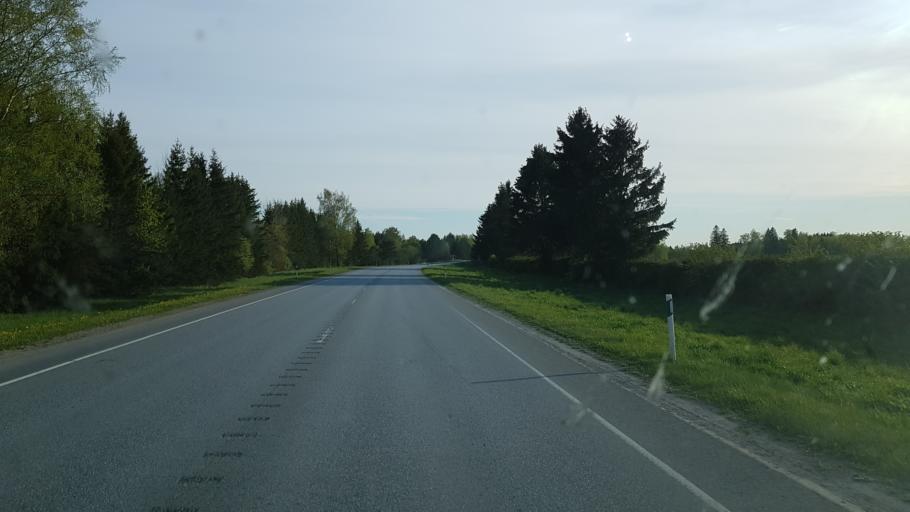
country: EE
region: Laeaene-Virumaa
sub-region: Viru-Nigula vald
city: Kunda
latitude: 59.3829
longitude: 26.6084
